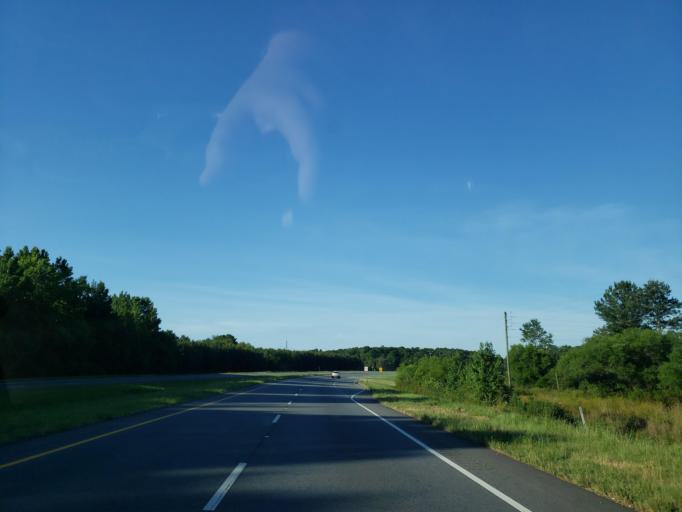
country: US
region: Georgia
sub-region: Floyd County
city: Shannon
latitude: 34.3519
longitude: -85.0714
